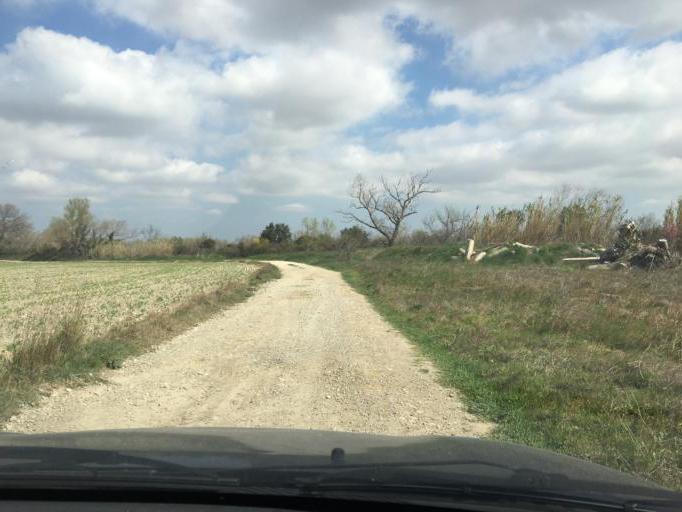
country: FR
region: Provence-Alpes-Cote d'Azur
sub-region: Departement du Vaucluse
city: Serignan-du-Comtat
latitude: 44.1688
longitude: 4.8266
